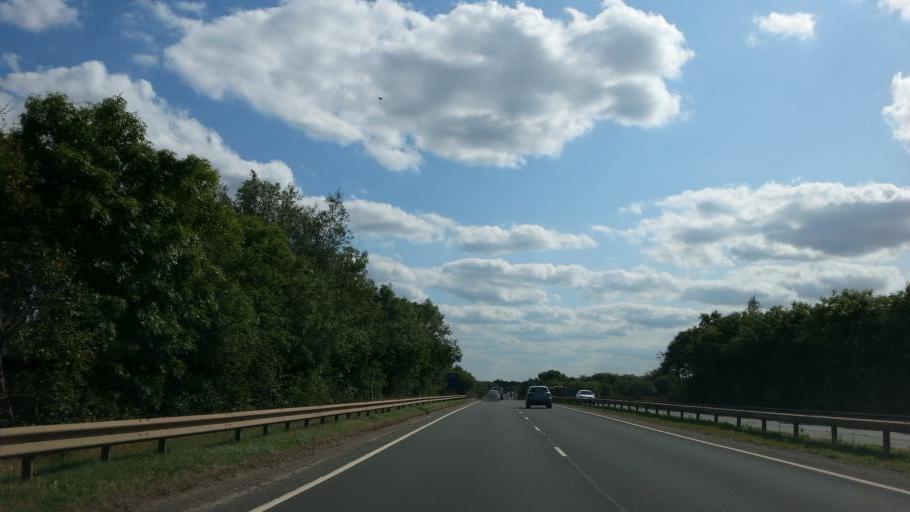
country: GB
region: England
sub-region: Leicestershire
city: Barrow upon Soar
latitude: 52.7333
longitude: -1.1352
